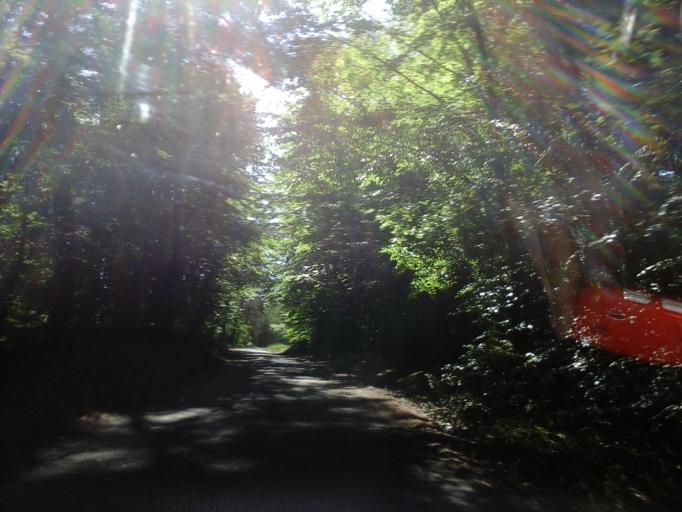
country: PL
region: West Pomeranian Voivodeship
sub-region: Powiat choszczenski
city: Drawno
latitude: 53.1391
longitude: 15.8832
